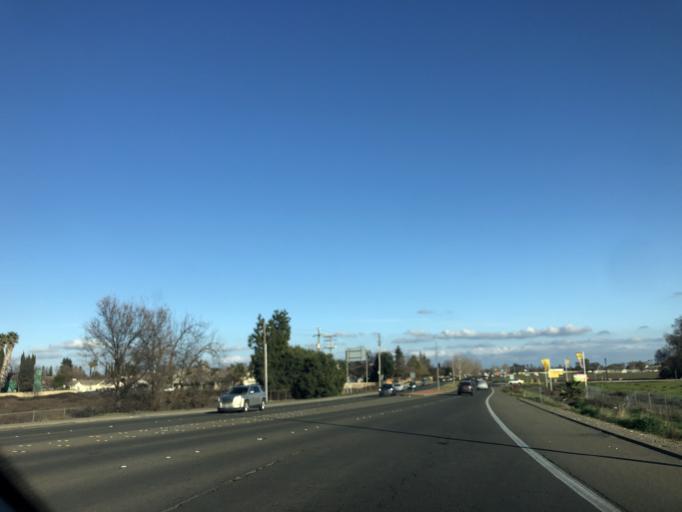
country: US
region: California
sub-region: Yolo County
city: Woodland
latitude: 38.6626
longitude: -121.7493
